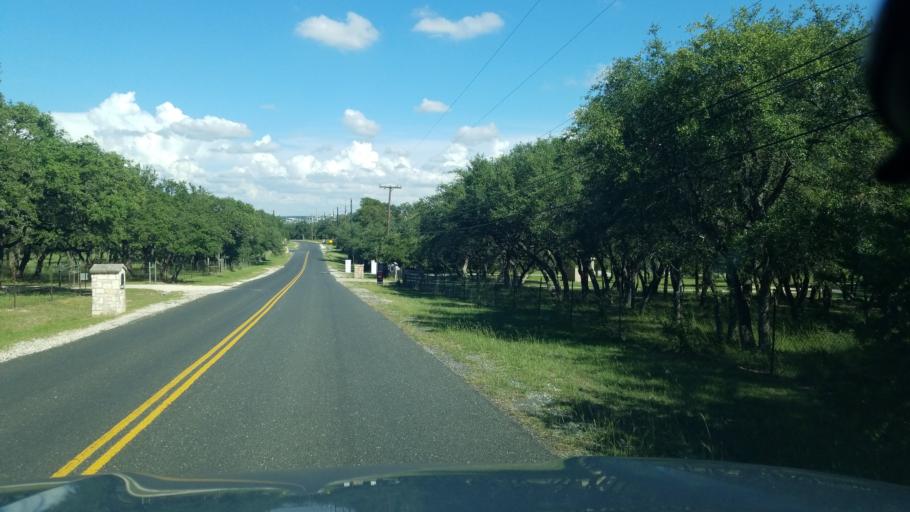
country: US
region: Texas
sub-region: Bexar County
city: Timberwood Park
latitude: 29.6765
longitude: -98.4989
